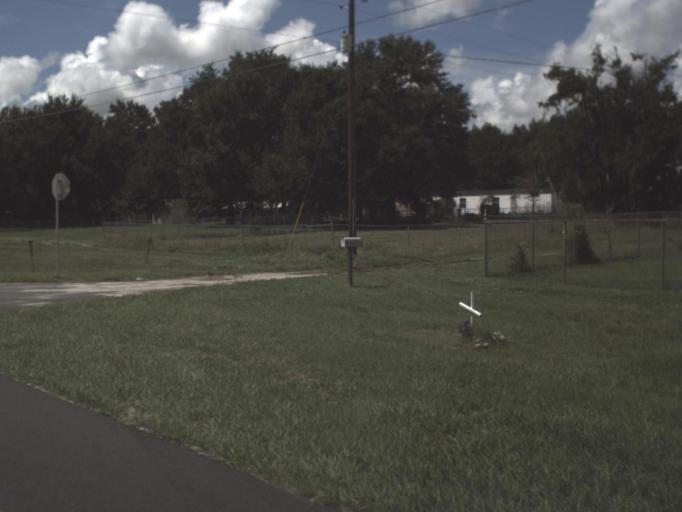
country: US
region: Florida
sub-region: Polk County
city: Polk City
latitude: 28.1722
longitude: -81.8548
